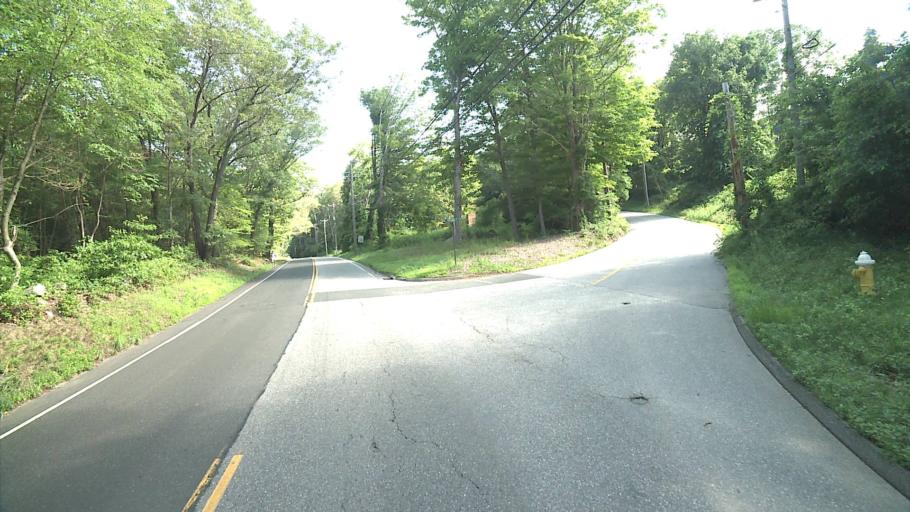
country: US
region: Connecticut
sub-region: Middlesex County
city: Westbrook Center
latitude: 41.3045
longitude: -72.4373
